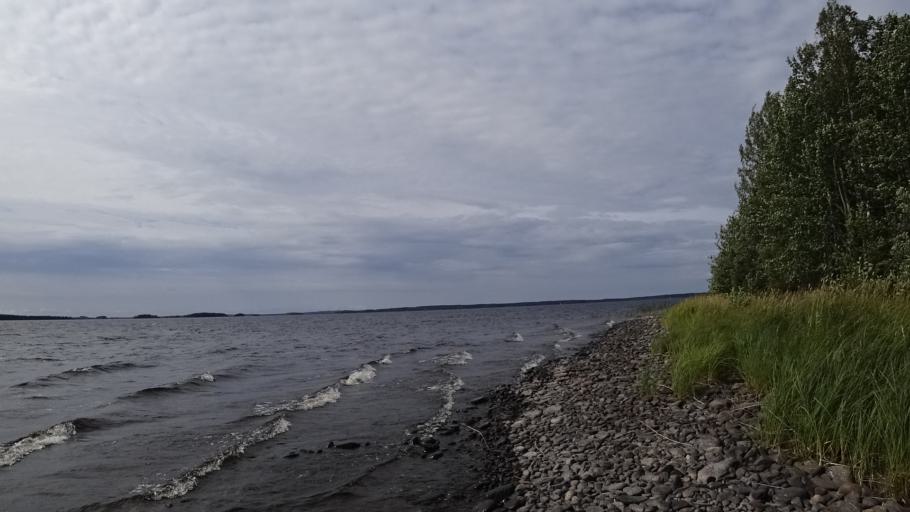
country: FI
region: North Karelia
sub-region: Keski-Karjala
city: Raeaekkylae
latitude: 62.3938
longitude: 29.7601
